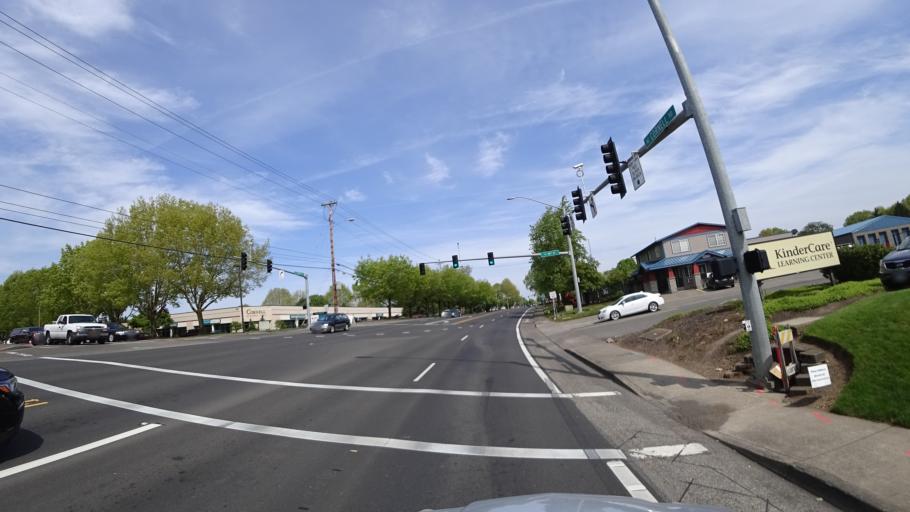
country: US
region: Oregon
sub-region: Washington County
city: Hillsboro
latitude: 45.5335
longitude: -122.9343
